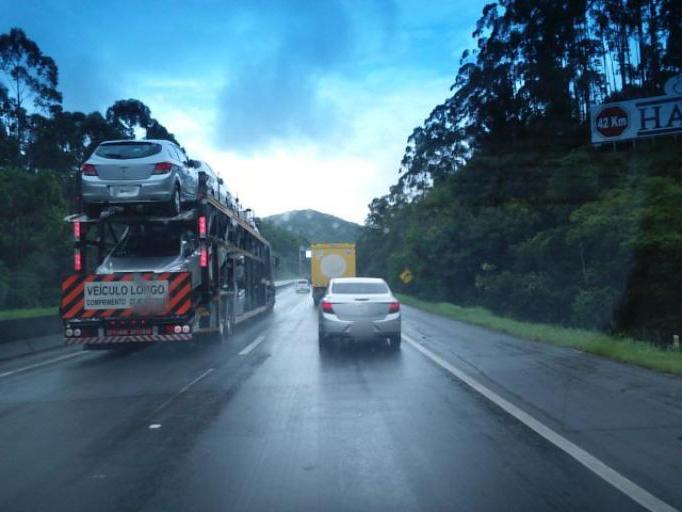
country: BR
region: Santa Catarina
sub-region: Balneario Camboriu
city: Balneario Camboriu
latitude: -26.9693
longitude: -48.6834
